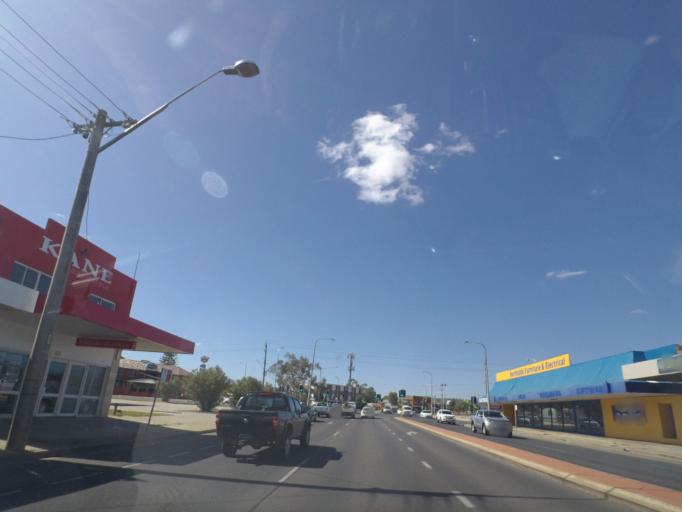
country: AU
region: New South Wales
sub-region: Albury Municipality
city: Lavington
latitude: -36.0531
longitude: 146.9334
